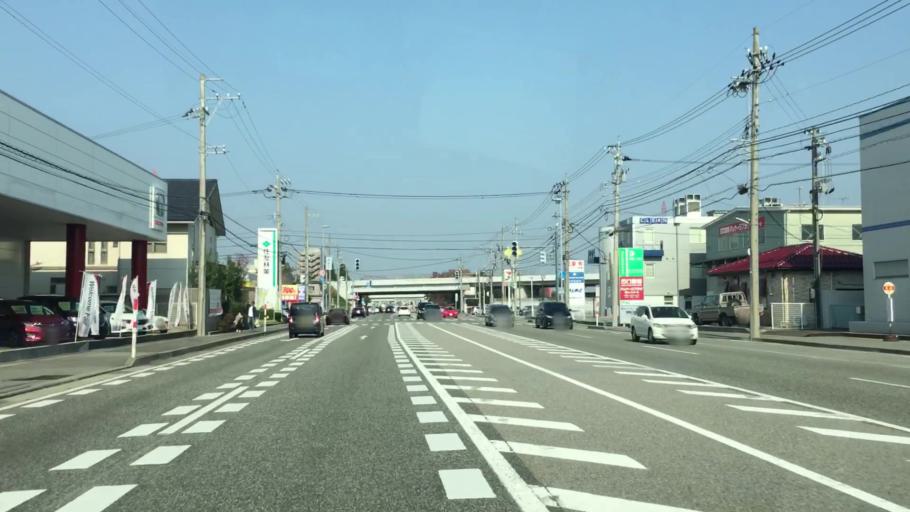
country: JP
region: Toyama
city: Toyama-shi
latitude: 36.6508
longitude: 137.2096
